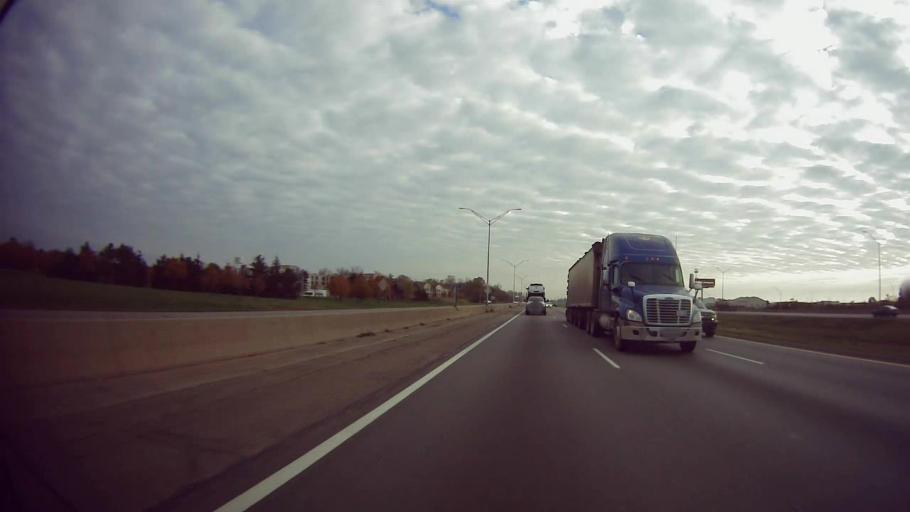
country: US
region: Michigan
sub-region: Wayne County
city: Romulus
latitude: 42.2398
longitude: -83.3396
